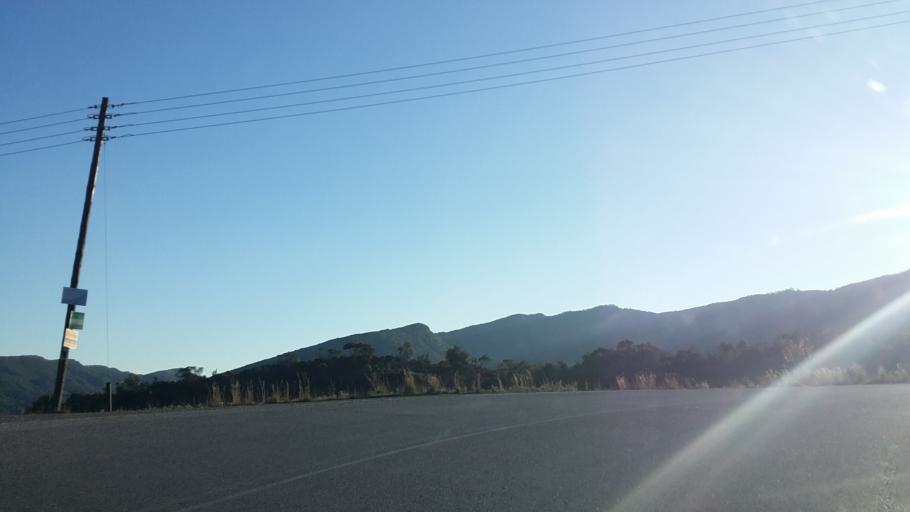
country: GR
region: West Greece
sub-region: Nomos Aitolias kai Akarnanias
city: Lepenou
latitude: 38.8366
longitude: 21.3295
